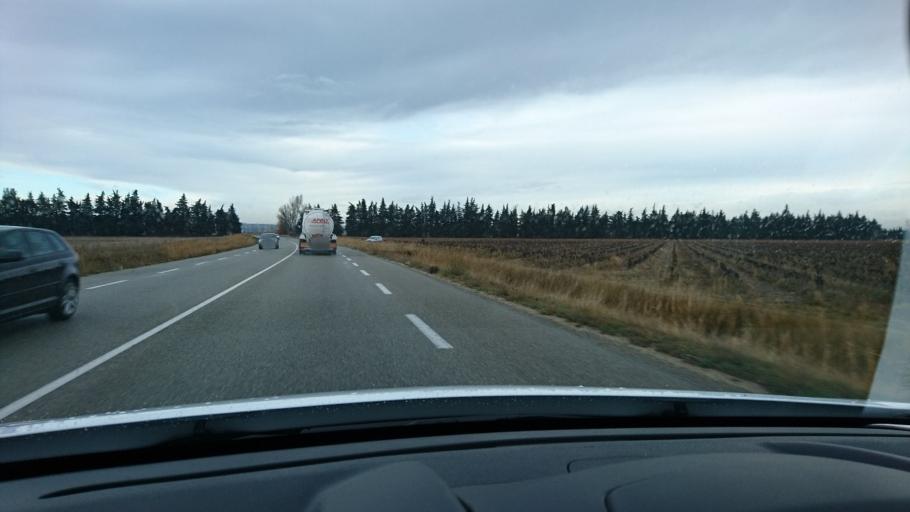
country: FR
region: Languedoc-Roussillon
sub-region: Departement du Gard
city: Les Angles
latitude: 43.9819
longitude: 4.7489
